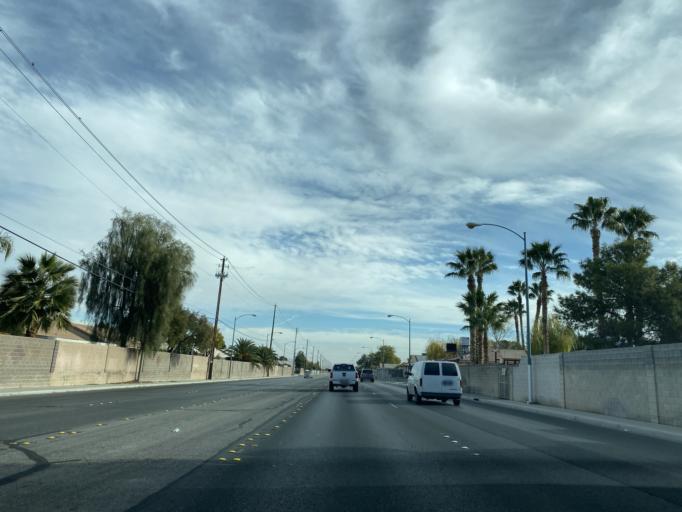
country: US
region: Nevada
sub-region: Clark County
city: Las Vegas
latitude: 36.2467
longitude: -115.2037
